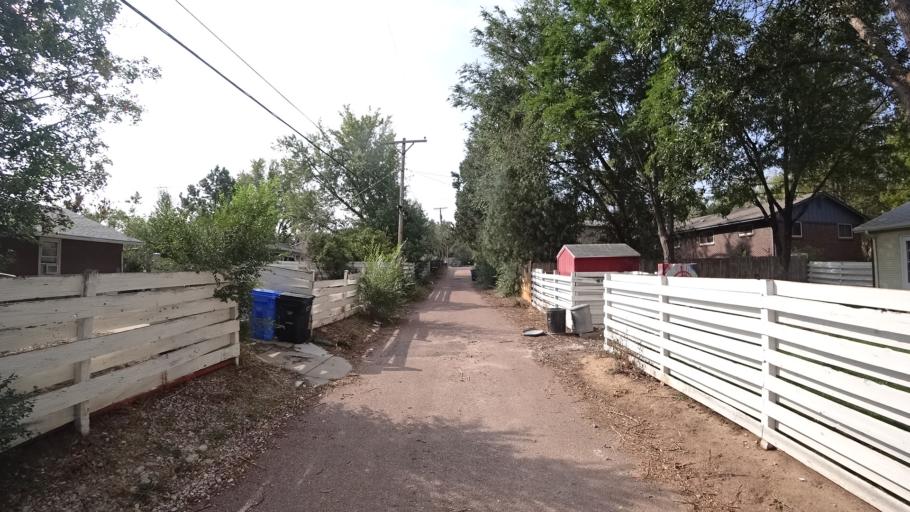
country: US
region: Colorado
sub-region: El Paso County
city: Colorado Springs
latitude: 38.8533
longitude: -104.7860
